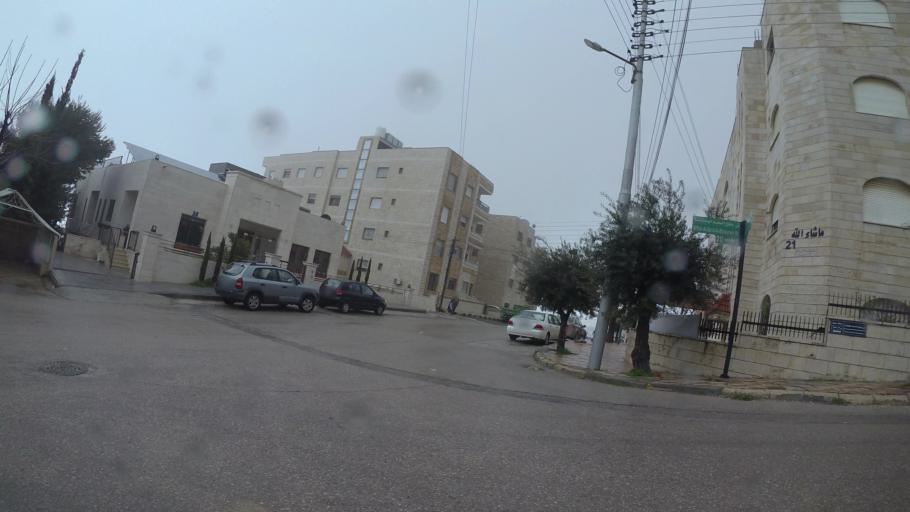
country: JO
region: Amman
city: Al Jubayhah
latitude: 32.0193
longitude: 35.8390
